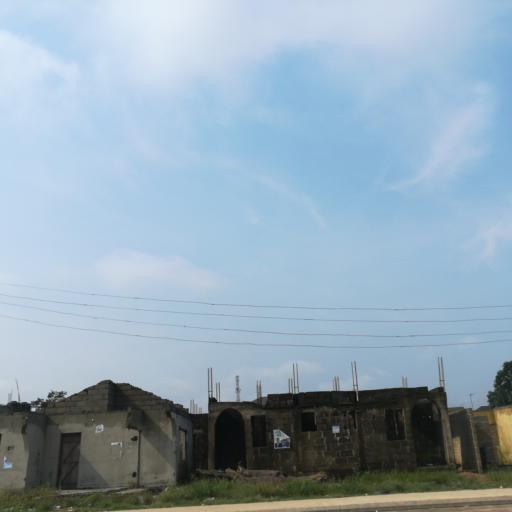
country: NG
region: Rivers
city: Port Harcourt
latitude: 4.8430
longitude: 7.0669
